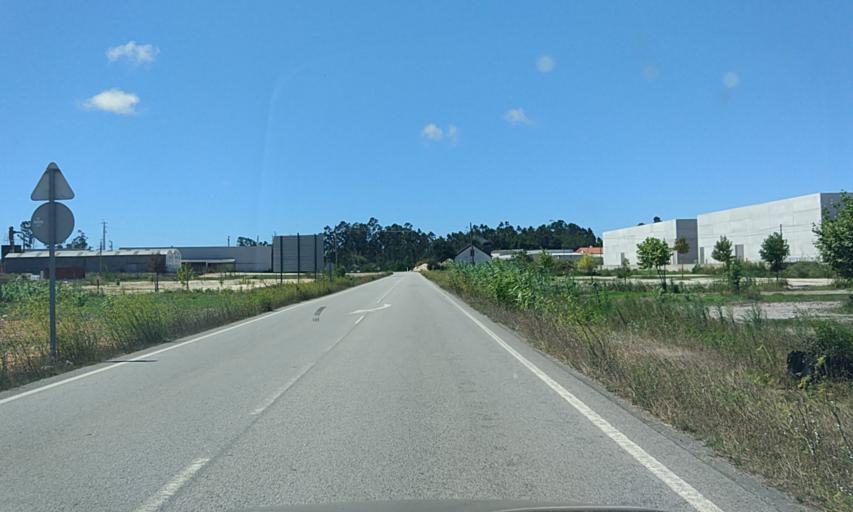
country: PT
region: Coimbra
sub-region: Mira
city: Mira
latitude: 40.4561
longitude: -8.7068
